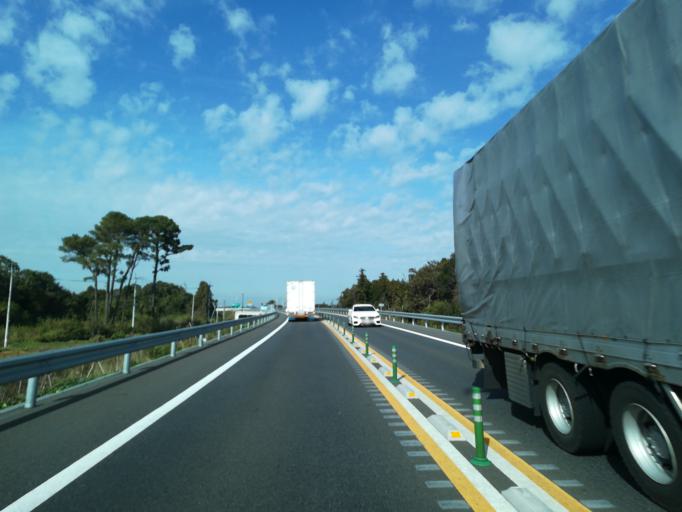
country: JP
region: Ibaraki
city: Ishige
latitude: 36.0752
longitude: 140.0130
